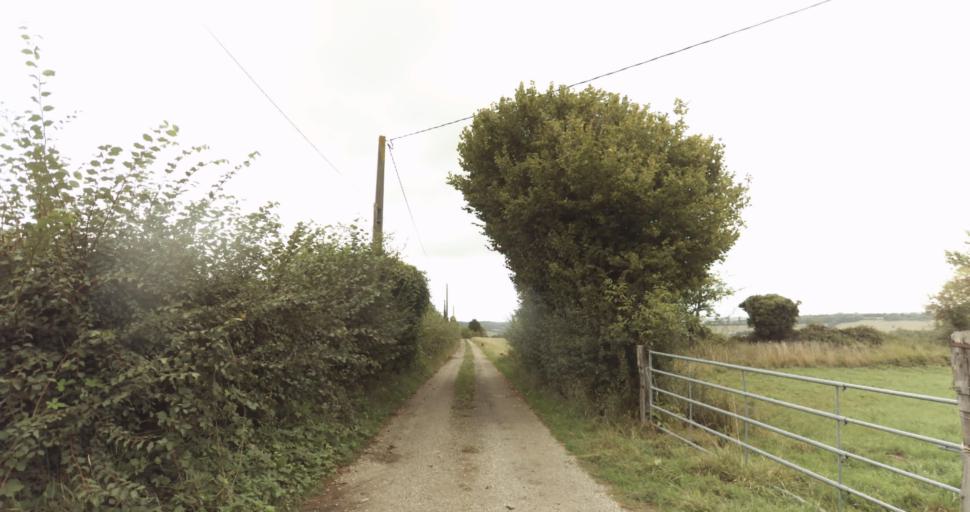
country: FR
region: Lower Normandy
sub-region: Departement de l'Orne
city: Gace
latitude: 48.7998
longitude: 0.2746
